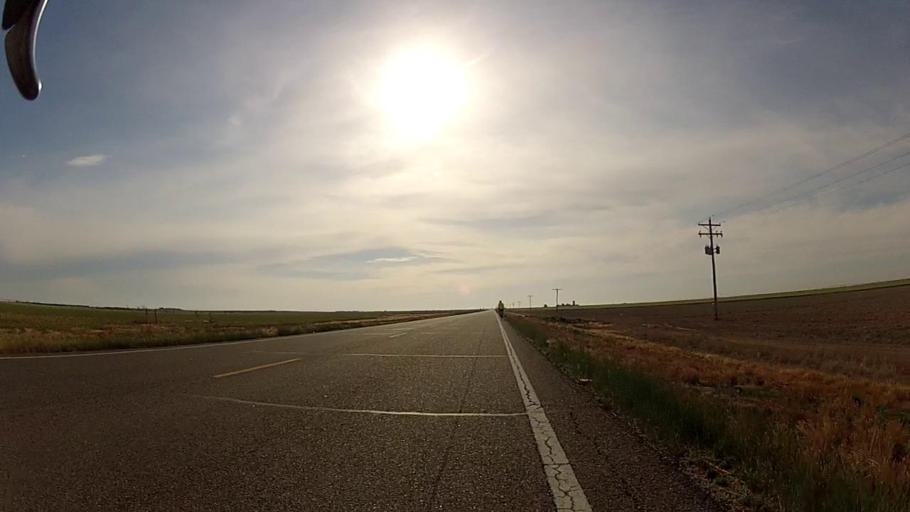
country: US
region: Kansas
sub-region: Grant County
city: Ulysses
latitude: 37.5766
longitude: -101.4632
